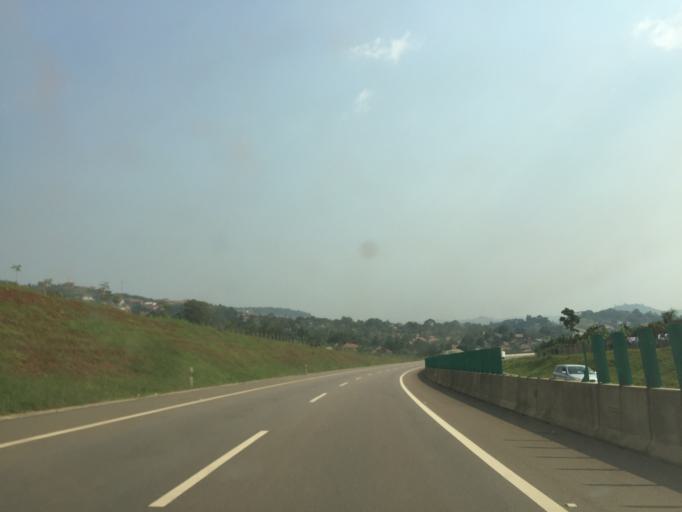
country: UG
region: Central Region
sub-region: Wakiso District
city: Kajansi
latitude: 0.2583
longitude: 32.5220
